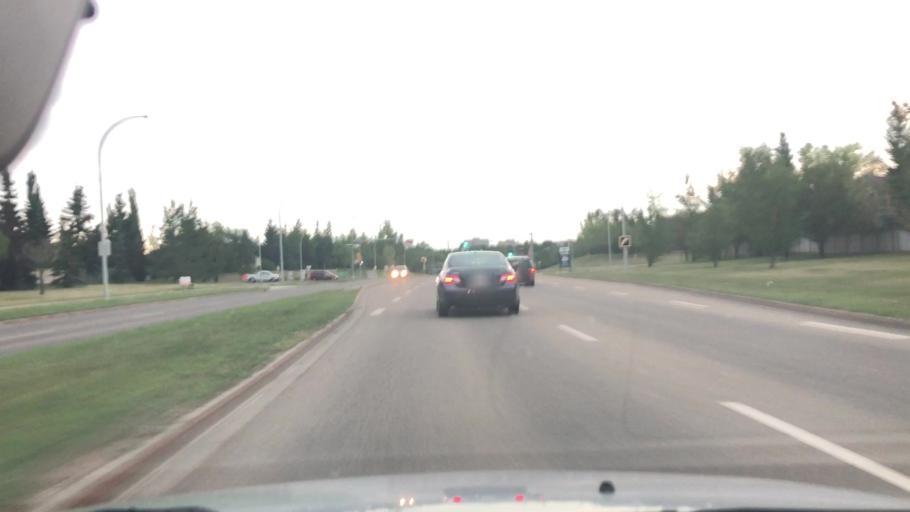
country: CA
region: Alberta
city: Edmonton
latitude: 53.4414
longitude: -113.5180
